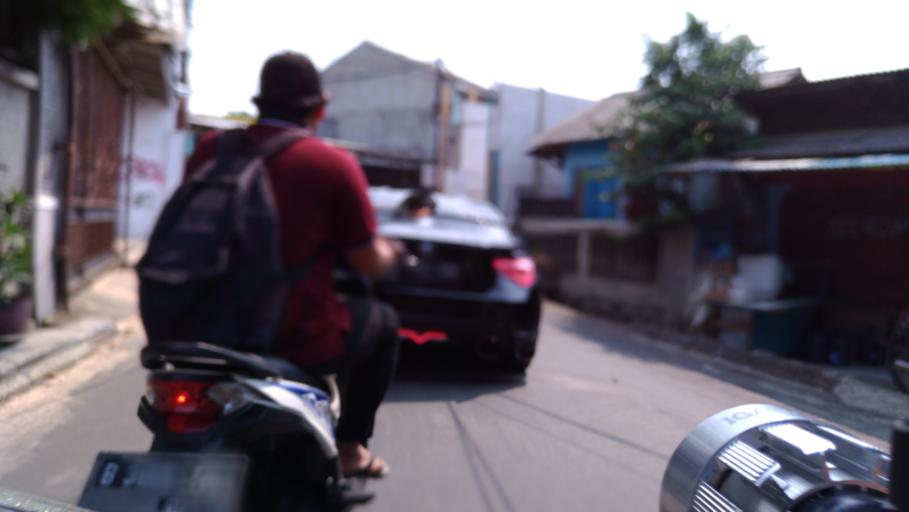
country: ID
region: West Java
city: Depok
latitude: -6.3540
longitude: 106.8736
